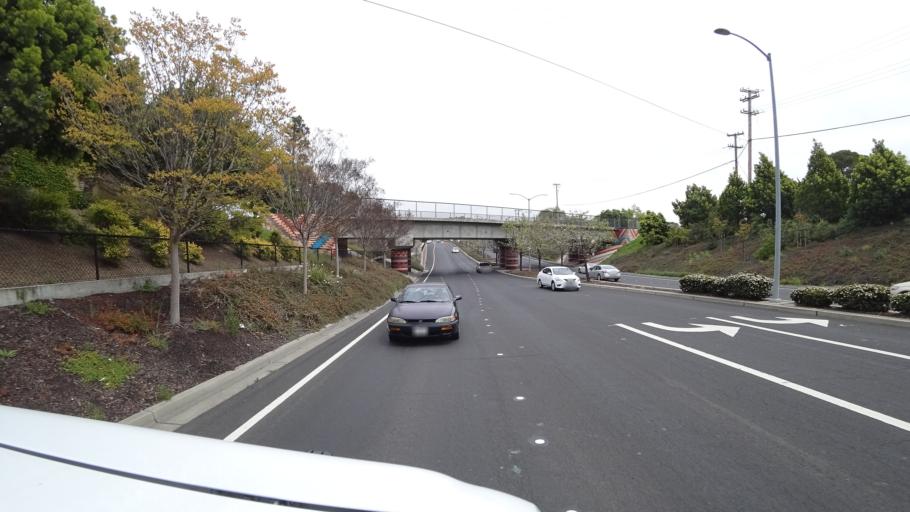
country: US
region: California
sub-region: Alameda County
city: Hayward
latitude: 37.6489
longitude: -122.0807
